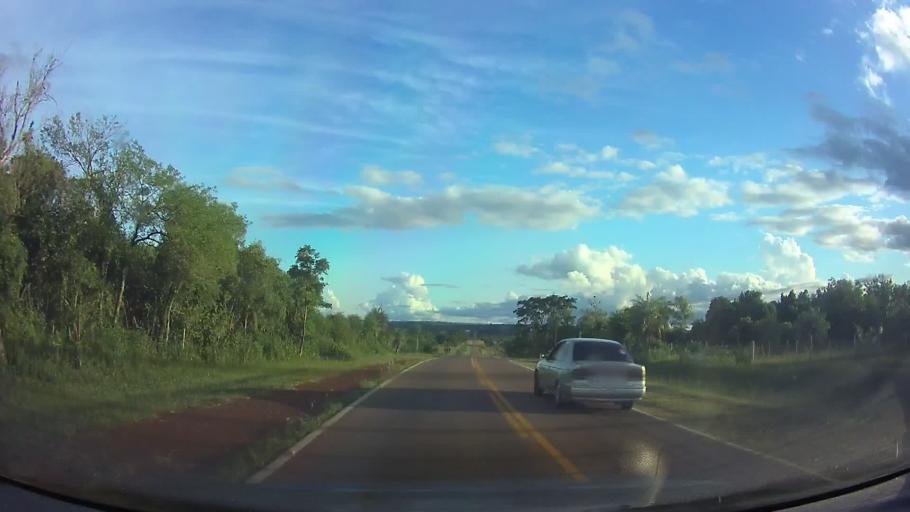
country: PY
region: Paraguari
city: Acahay
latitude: -25.8741
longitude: -57.1245
